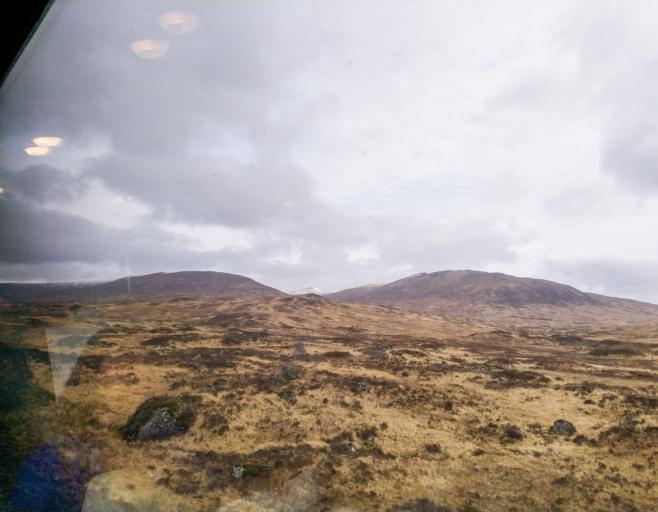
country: GB
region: Scotland
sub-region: Highland
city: Spean Bridge
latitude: 56.6951
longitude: -4.5739
